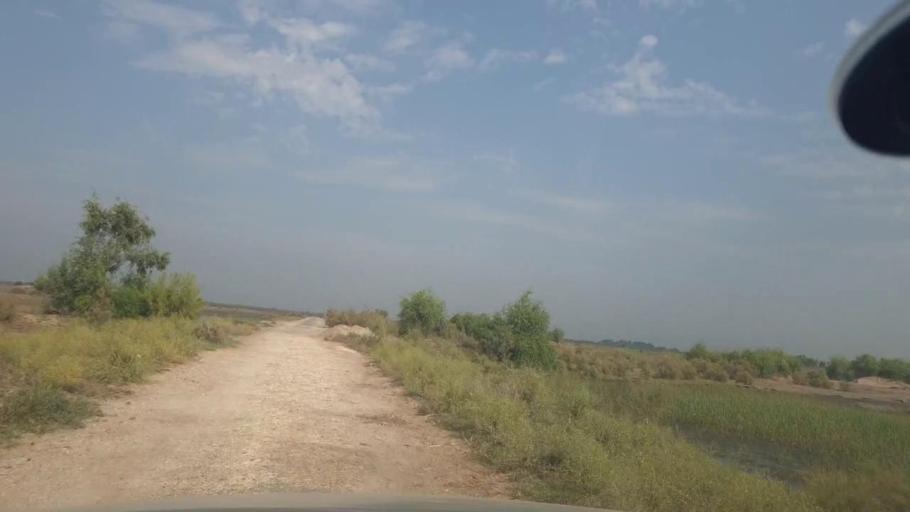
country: PK
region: Balochistan
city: Mehrabpur
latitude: 28.0359
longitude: 68.1274
